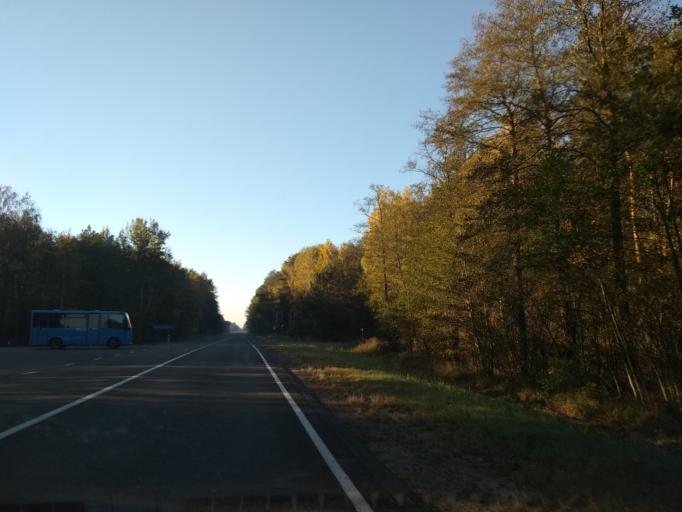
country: BY
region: Brest
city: Kobryn
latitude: 52.0608
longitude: 24.2823
